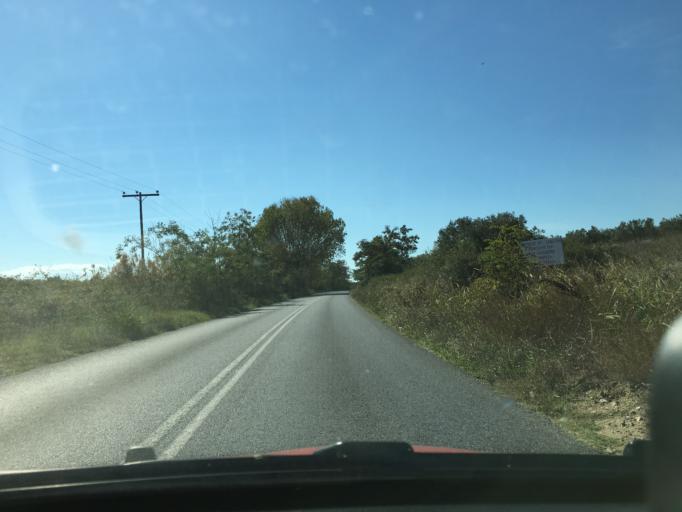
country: GR
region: Central Macedonia
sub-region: Nomos Chalkidikis
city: Nea Roda
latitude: 40.3739
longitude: 23.9244
